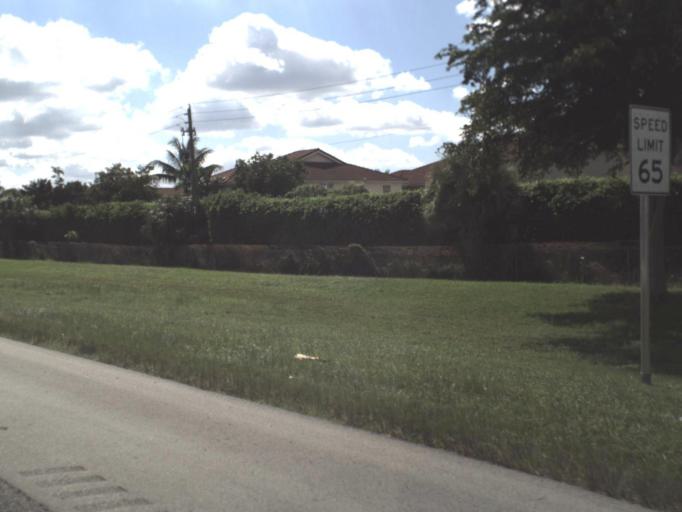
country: US
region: Florida
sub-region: Palm Beach County
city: Boca Pointe
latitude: 26.2935
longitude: -80.1693
